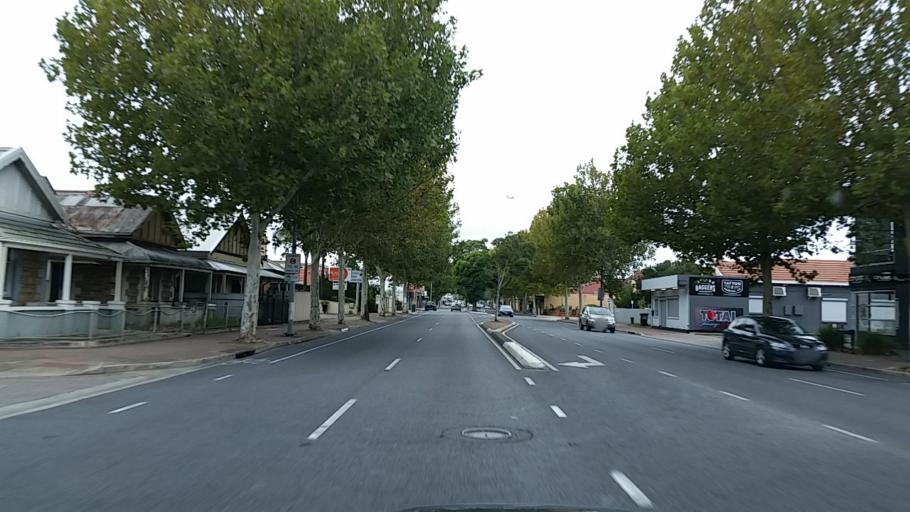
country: AU
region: South Australia
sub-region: City of West Torrens
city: Thebarton
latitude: -34.9245
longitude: 138.5540
